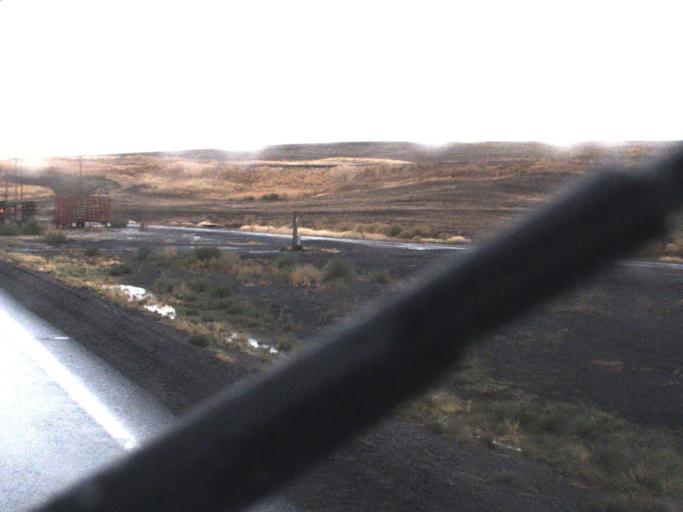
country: US
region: Washington
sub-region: Whitman County
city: Colfax
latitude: 47.0934
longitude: -117.5864
